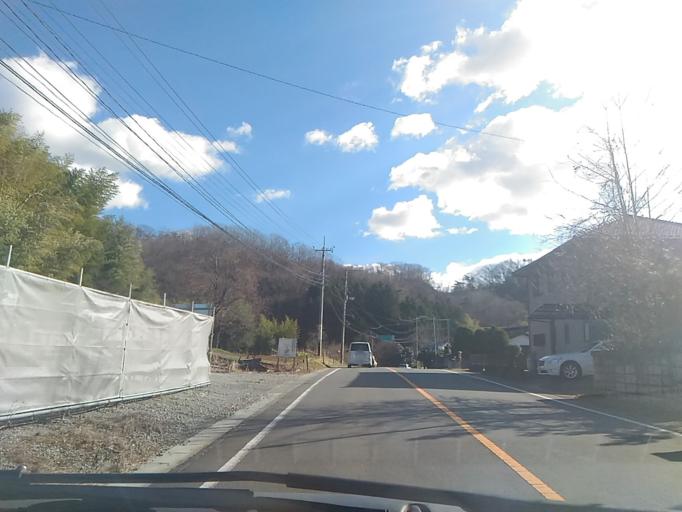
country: JP
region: Fukushima
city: Iwaki
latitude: 37.0034
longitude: 140.7875
